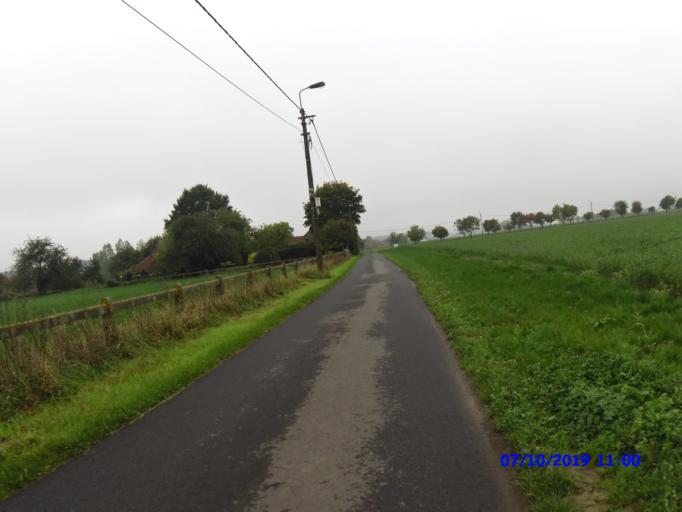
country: BE
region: Flanders
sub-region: Provincie Oost-Vlaanderen
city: Oosterzele
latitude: 50.9744
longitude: 3.7831
